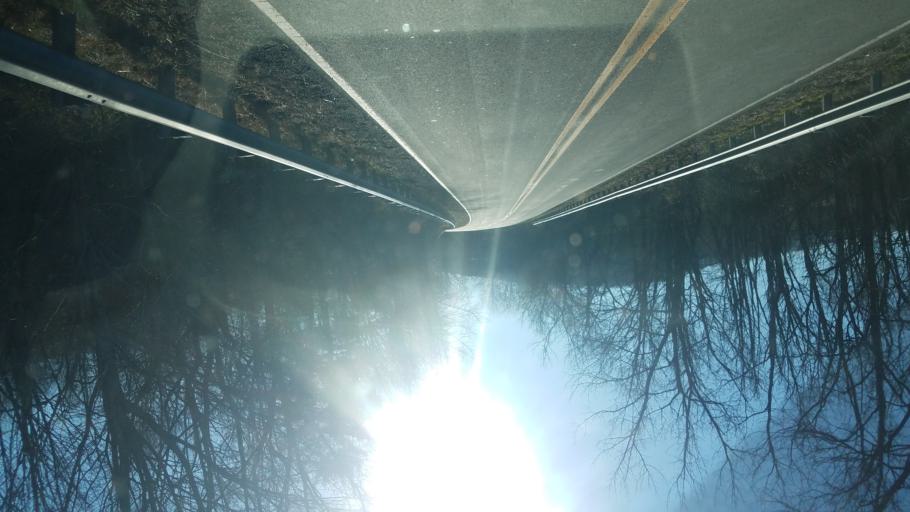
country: US
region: Virginia
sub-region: Pulaski County
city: Pulaski
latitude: 37.1693
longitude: -80.8924
